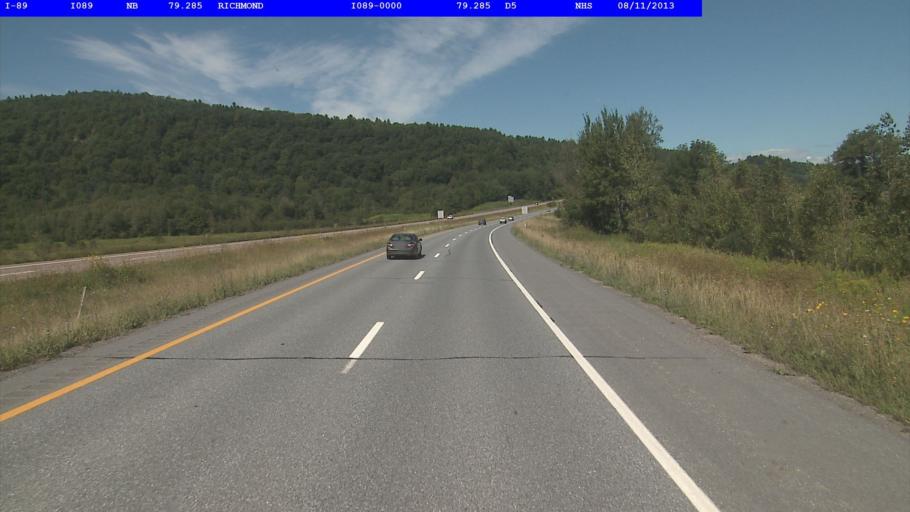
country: US
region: Vermont
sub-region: Chittenden County
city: Williston
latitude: 44.4226
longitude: -73.0270
